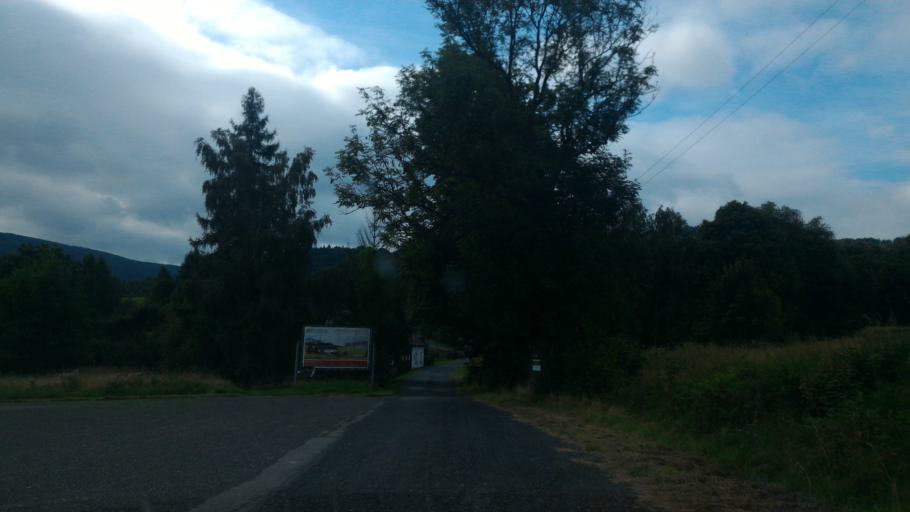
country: CZ
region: Ustecky
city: Dolni Podluzi
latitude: 50.8685
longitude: 14.5768
